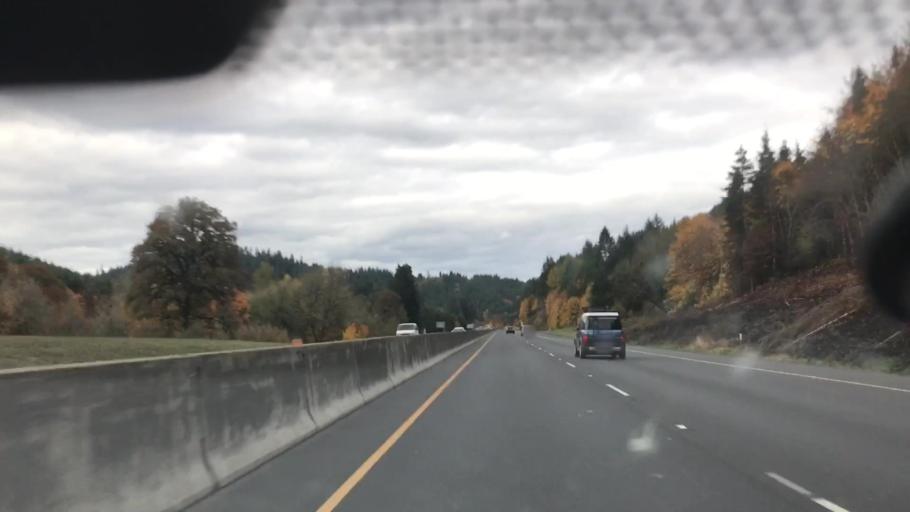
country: US
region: Oregon
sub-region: Douglas County
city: Drain
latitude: 43.7264
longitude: -123.2039
